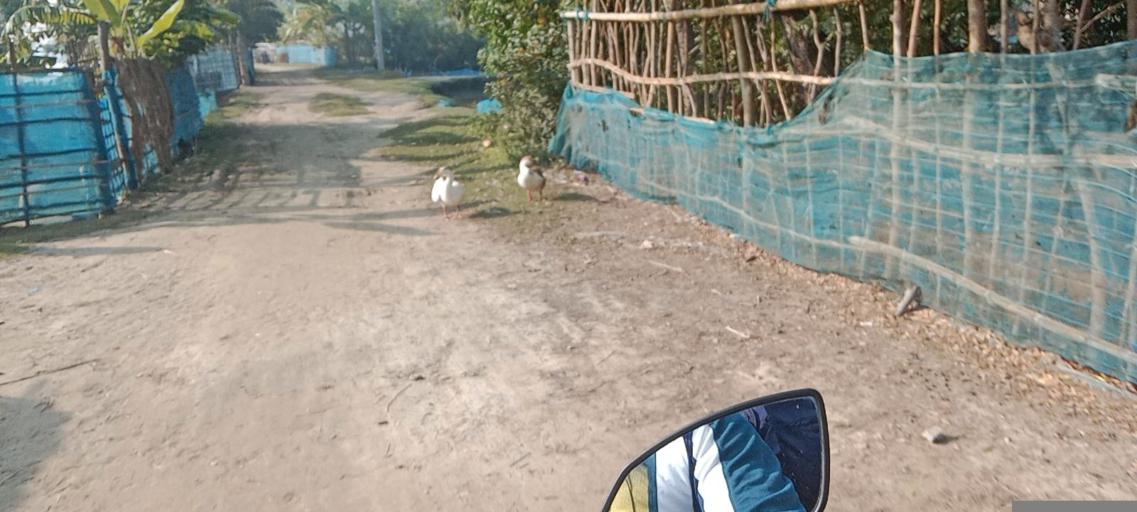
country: BD
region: Khulna
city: Phultala
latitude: 22.6086
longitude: 89.5879
